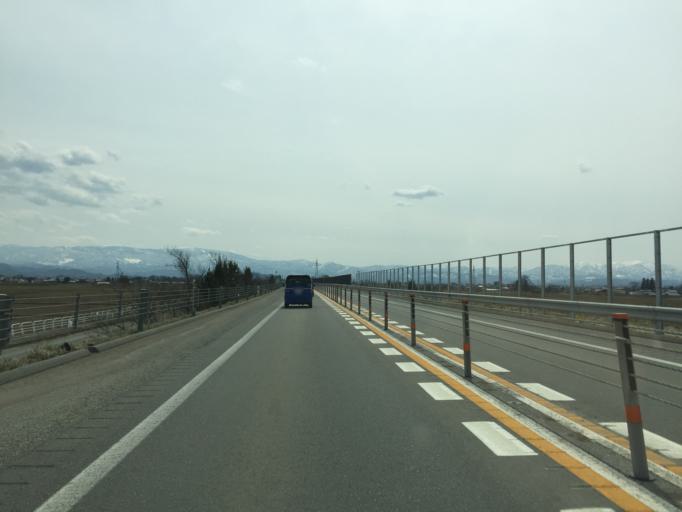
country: JP
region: Yamagata
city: Takahata
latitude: 38.0160
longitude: 140.1579
